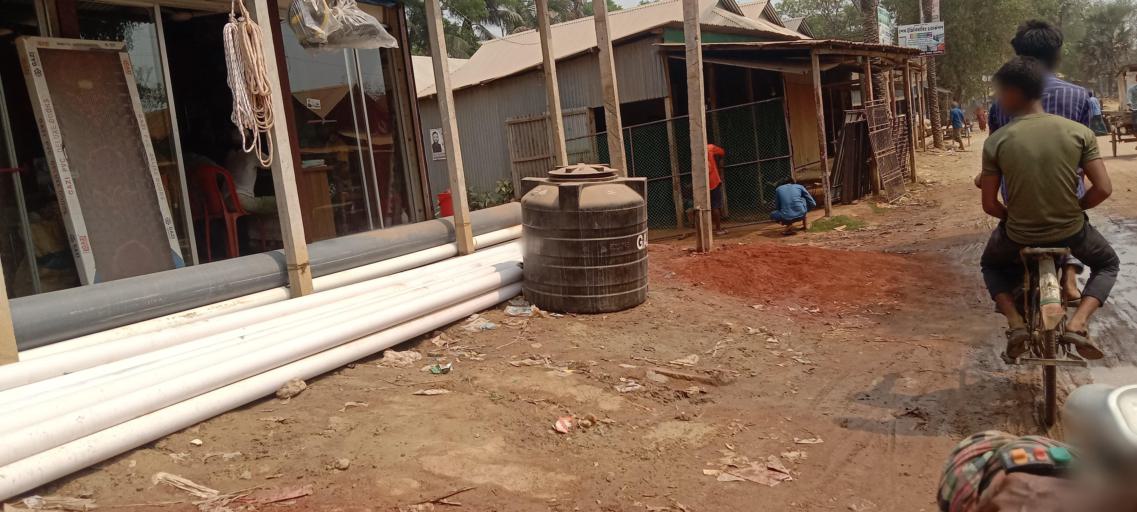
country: BD
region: Dhaka
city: Sakhipur
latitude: 24.3090
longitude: 90.2699
